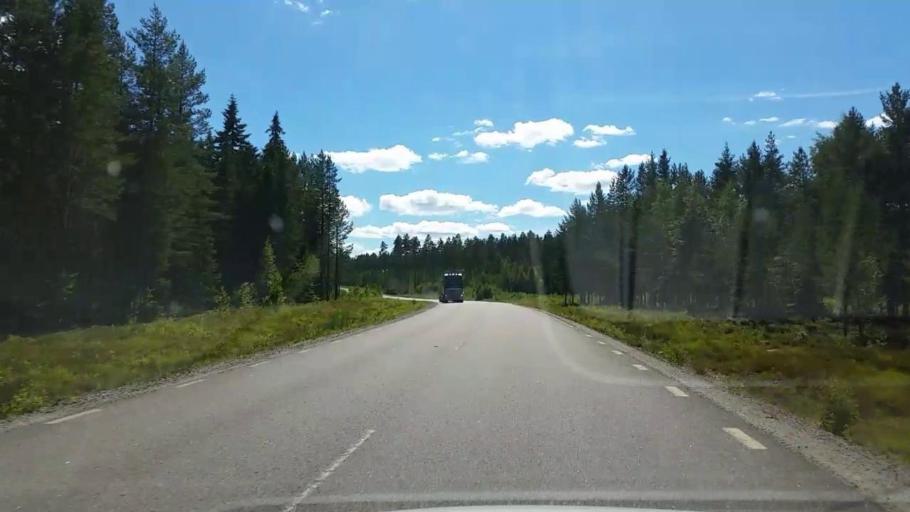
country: SE
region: Dalarna
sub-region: Faluns Kommun
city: Svardsjo
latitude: 61.0289
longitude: 15.7628
